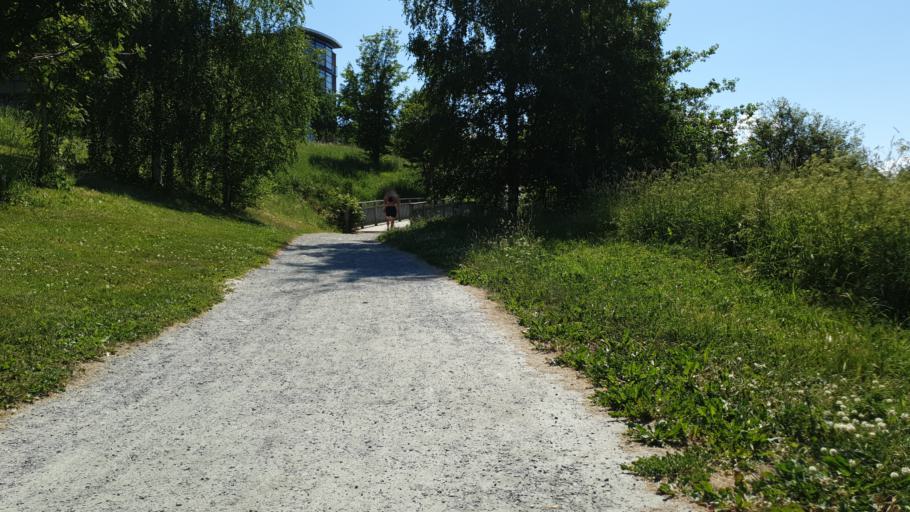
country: NO
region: Sor-Trondelag
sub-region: Trondheim
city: Trondheim
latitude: 63.4396
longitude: 10.4762
